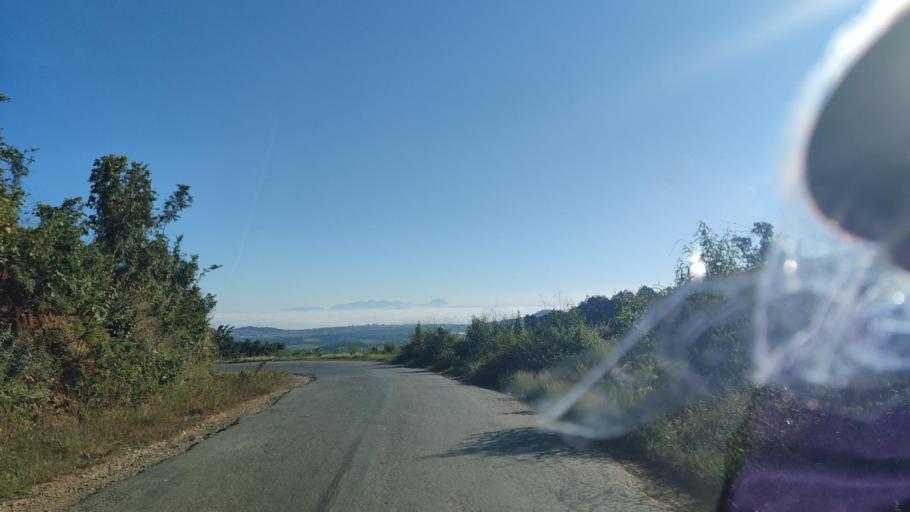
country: MM
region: Shan
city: Taunggyi
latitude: 20.9273
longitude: 97.6040
